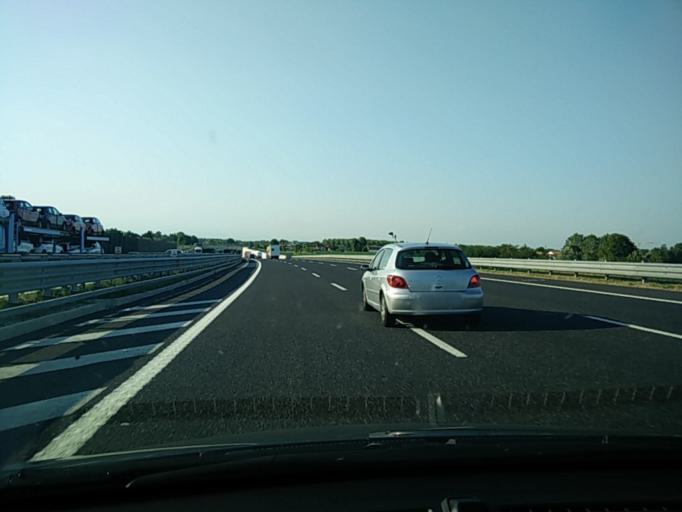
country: IT
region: Veneto
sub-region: Provincia di Venezia
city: Maerne
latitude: 45.5316
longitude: 12.1416
